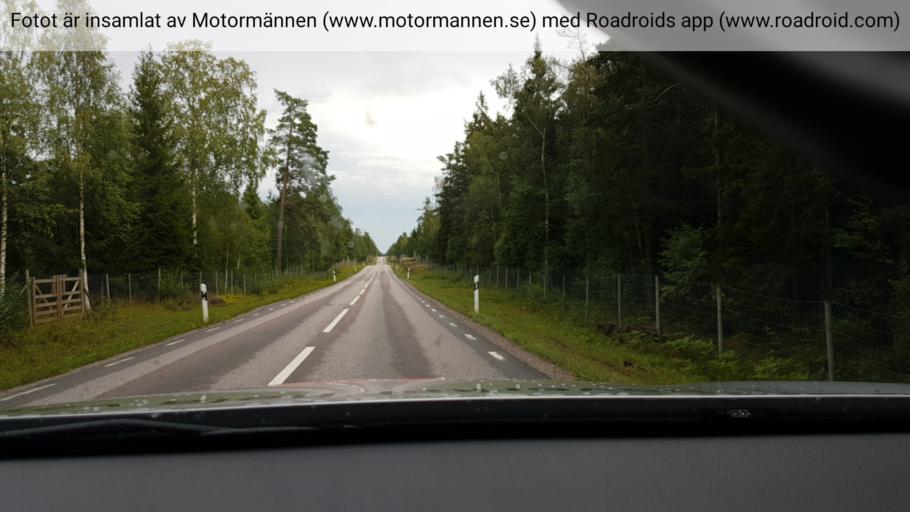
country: SE
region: Uppsala
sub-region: Osthammars Kommun
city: Osterbybruk
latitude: 60.3785
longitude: 17.9943
